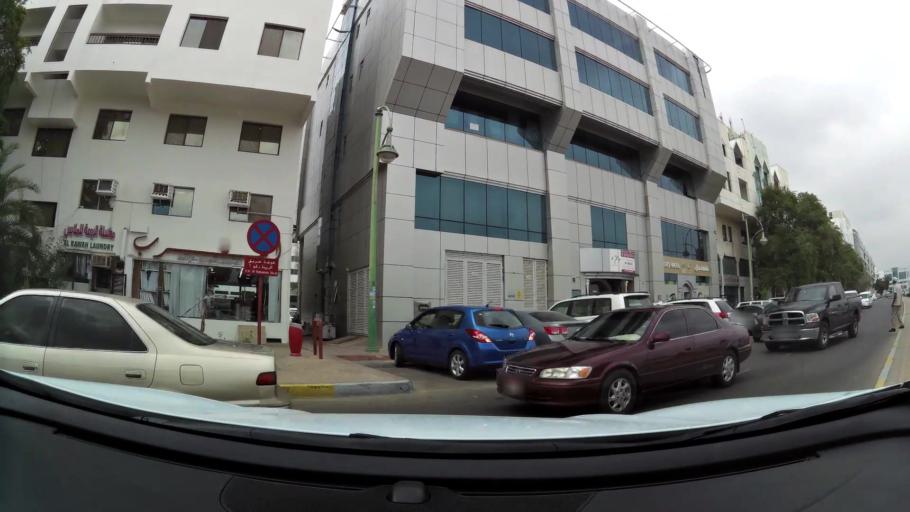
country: AE
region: Abu Dhabi
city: Al Ain
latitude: 24.2166
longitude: 55.7606
